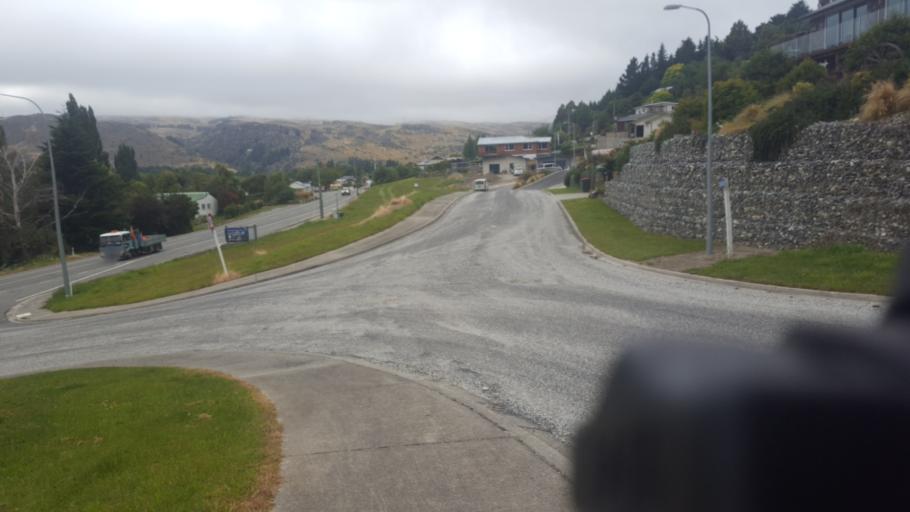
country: NZ
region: Otago
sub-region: Queenstown-Lakes District
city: Kingston
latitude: -45.5344
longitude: 169.3012
